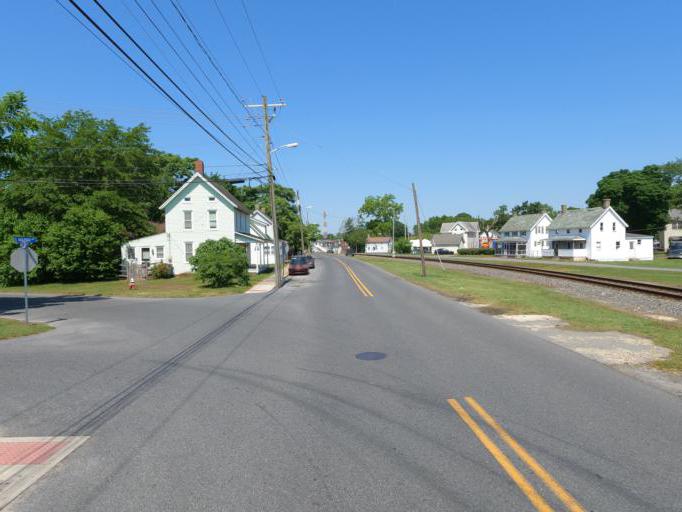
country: US
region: Delaware
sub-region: Sussex County
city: Georgetown
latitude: 38.6911
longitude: -75.3804
